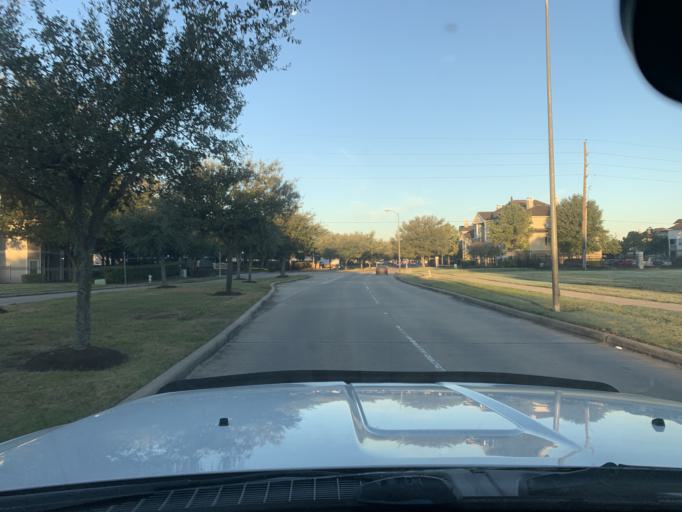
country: US
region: Texas
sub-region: Fort Bend County
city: Four Corners
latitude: 29.6483
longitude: -95.6472
